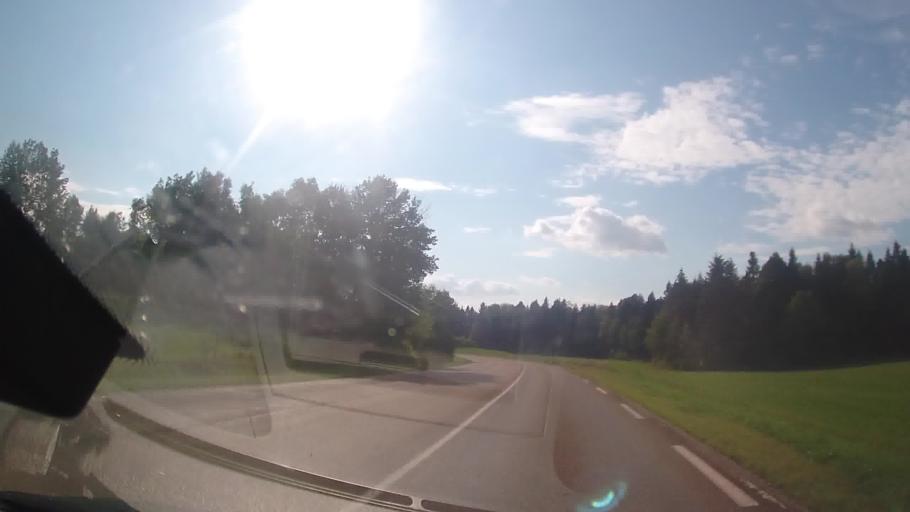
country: FR
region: Franche-Comte
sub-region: Departement du Jura
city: Clairvaux-les-Lacs
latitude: 46.5823
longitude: 5.7906
